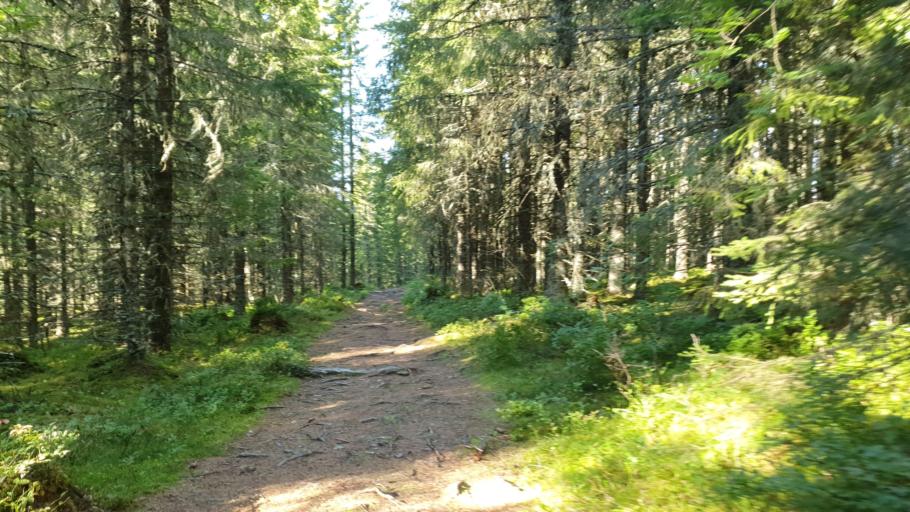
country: NO
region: Nord-Trondelag
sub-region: Levanger
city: Levanger
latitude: 63.6948
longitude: 11.2762
